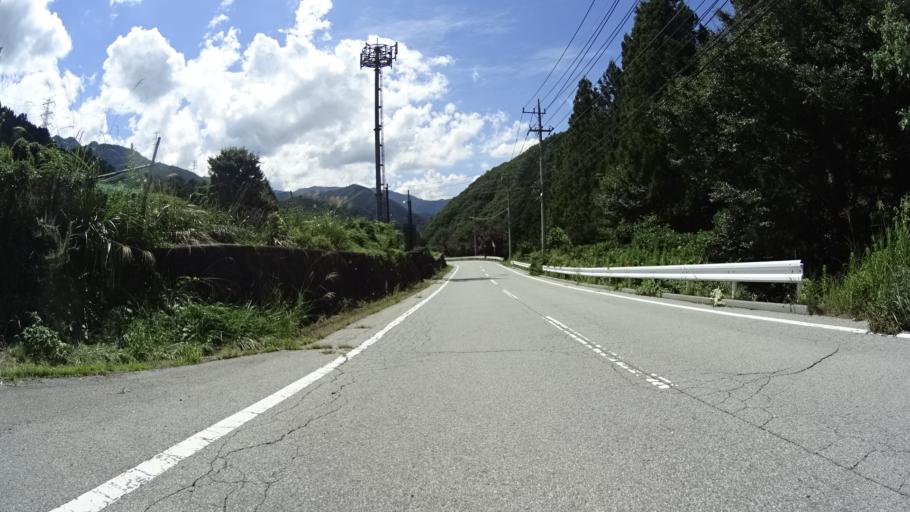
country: JP
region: Yamanashi
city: Enzan
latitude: 35.6446
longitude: 138.8070
